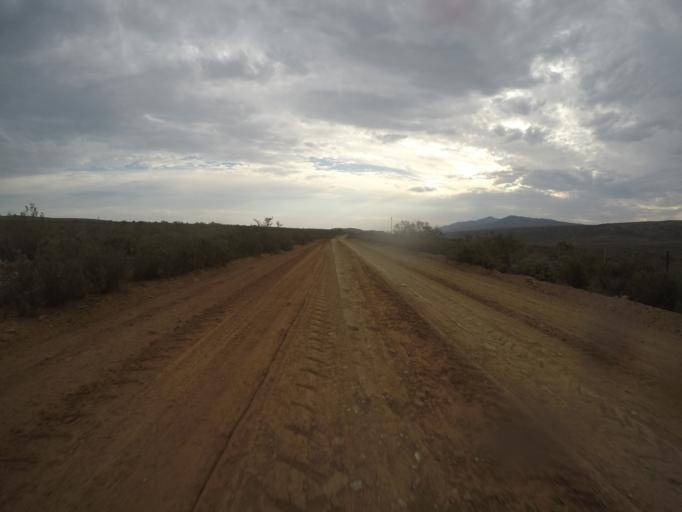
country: ZA
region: Eastern Cape
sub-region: Cacadu District Municipality
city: Willowmore
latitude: -33.4924
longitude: 23.5808
